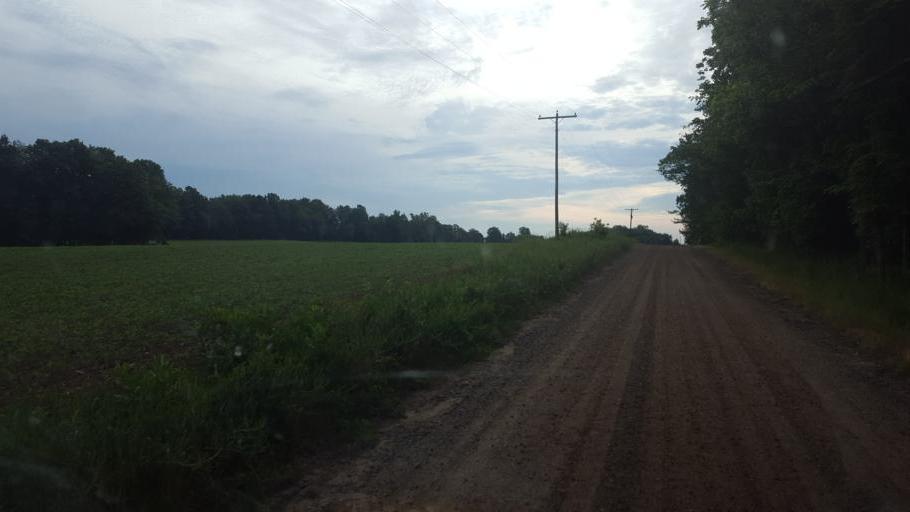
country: US
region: Michigan
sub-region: Eaton County
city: Charlotte
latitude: 42.6117
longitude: -84.8944
